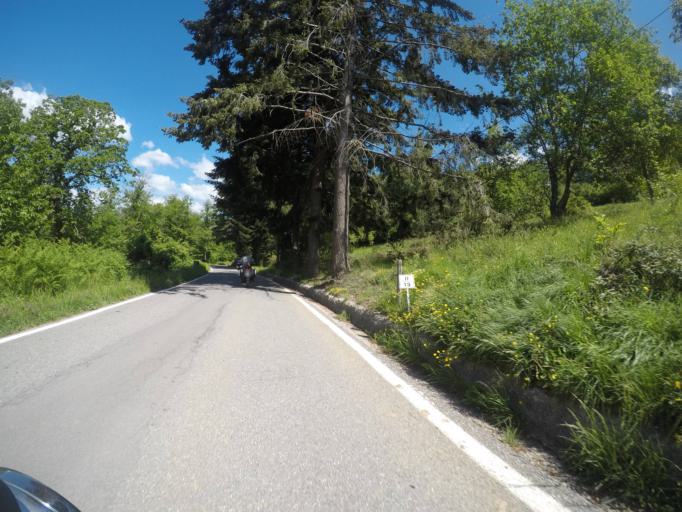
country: IT
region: Tuscany
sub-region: Provincia di Lucca
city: Careggine
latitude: 44.1093
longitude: 10.3329
